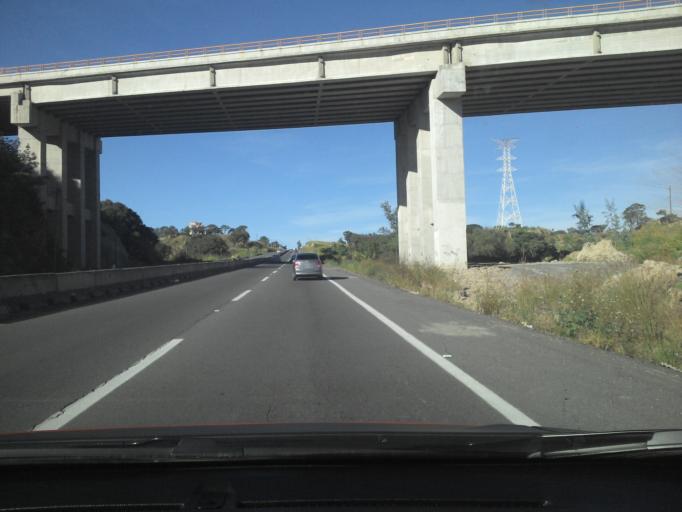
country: MX
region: Jalisco
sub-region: Tala
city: Los Ruisenores
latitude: 20.6892
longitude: -103.6926
